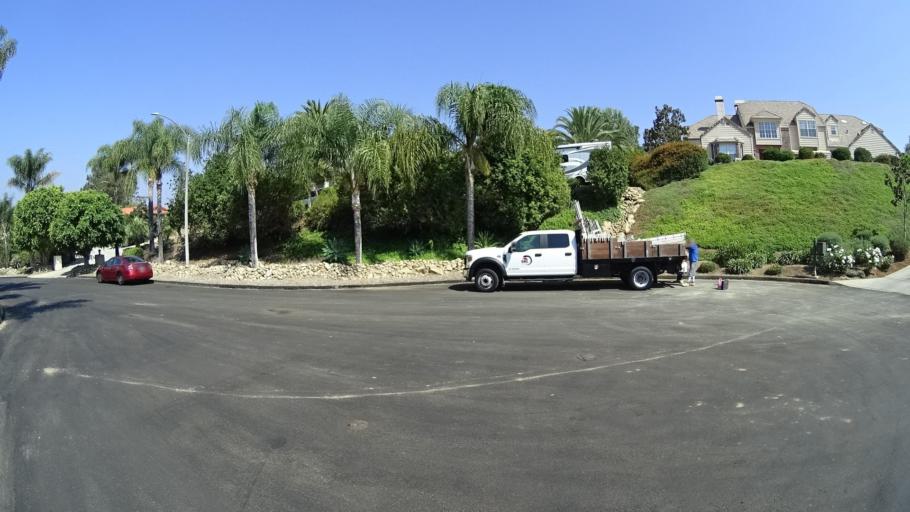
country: US
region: California
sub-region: San Diego County
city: Bonsall
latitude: 33.2558
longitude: -117.1895
